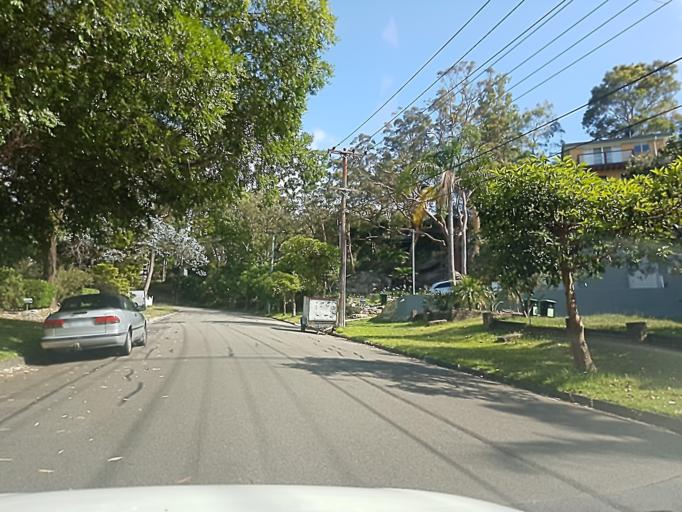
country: AU
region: New South Wales
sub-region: Warringah
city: Davidson
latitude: -33.7438
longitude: 151.2111
